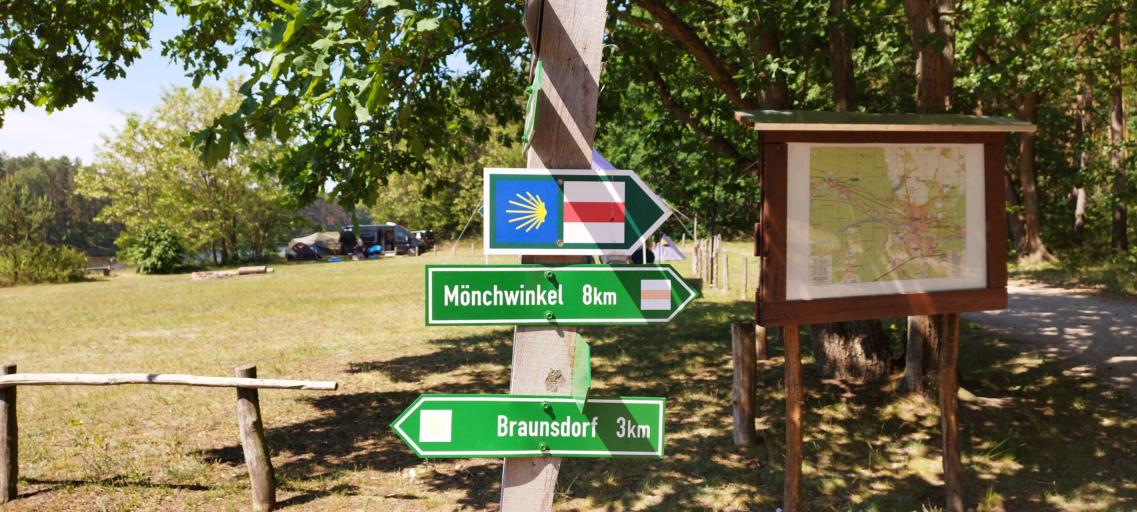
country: DE
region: Brandenburg
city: Rauen
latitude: 52.3684
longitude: 13.9925
